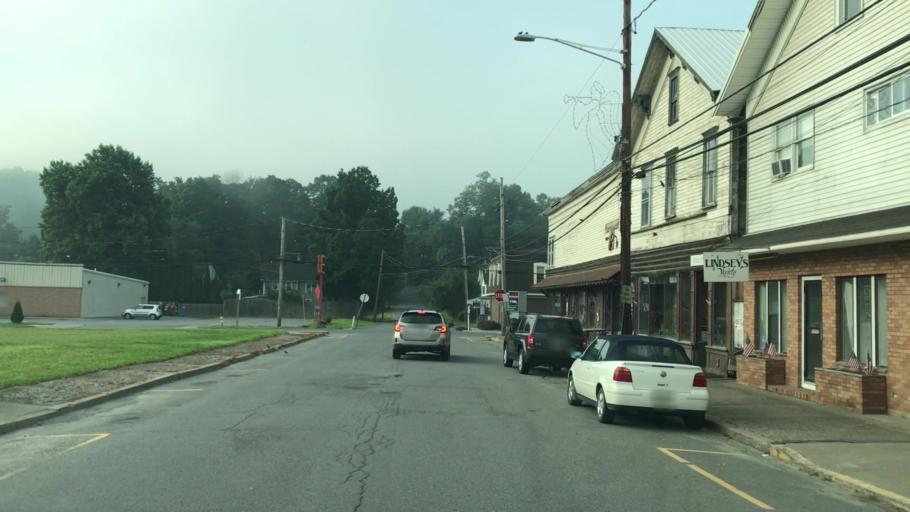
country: US
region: Pennsylvania
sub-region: Wyoming County
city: Factoryville
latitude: 41.6257
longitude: -75.7806
